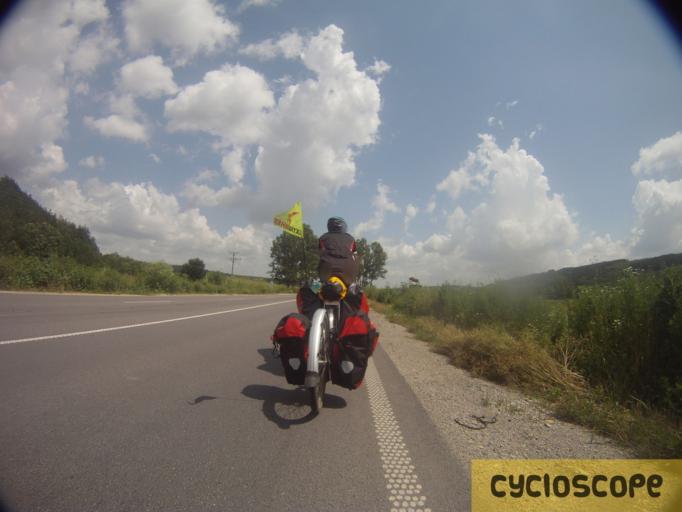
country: BG
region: Razgrad
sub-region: Obshtina Razgrad
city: Razgrad
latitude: 43.5128
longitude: 26.5815
